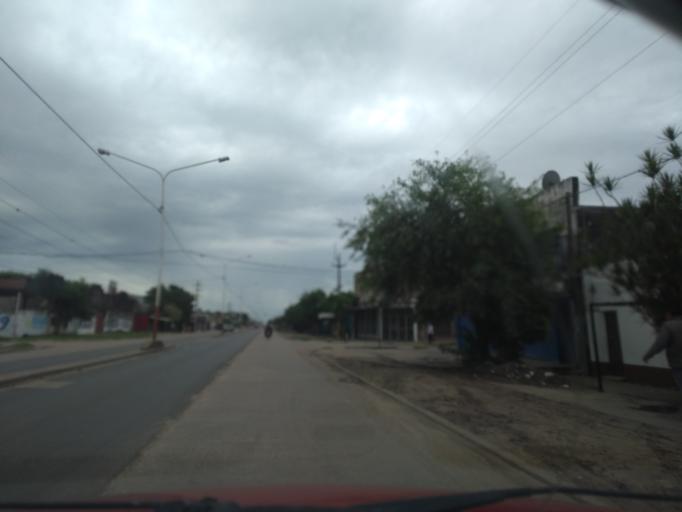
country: AR
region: Chaco
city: Resistencia
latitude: -27.4817
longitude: -58.9663
